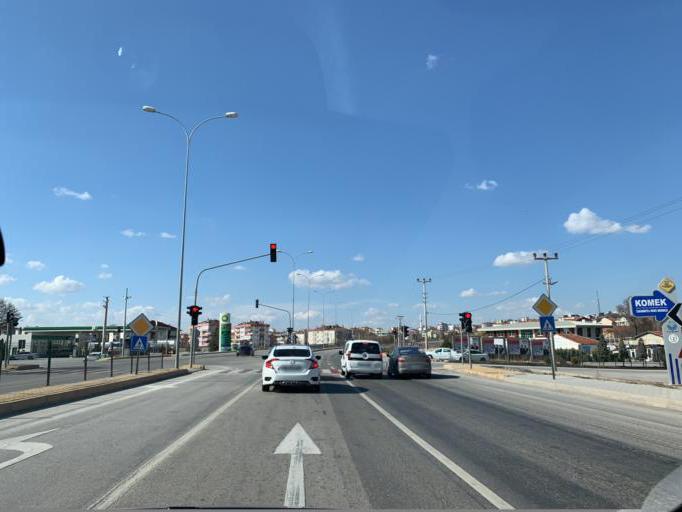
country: TR
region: Konya
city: Cihanbeyli
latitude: 38.6553
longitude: 32.9190
